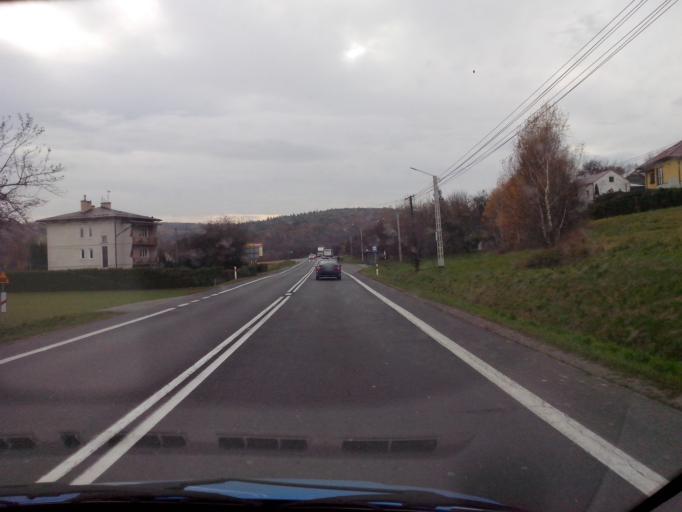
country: PL
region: Subcarpathian Voivodeship
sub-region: Powiat rzeszowski
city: Lubenia
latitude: 49.9401
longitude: 21.9074
